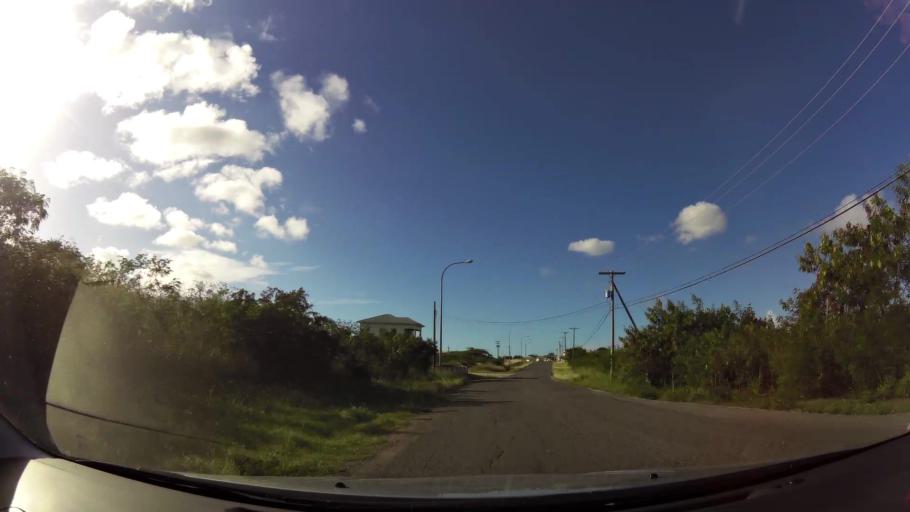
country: AG
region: Saint George
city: Piggotts
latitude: 17.1137
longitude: -61.8030
